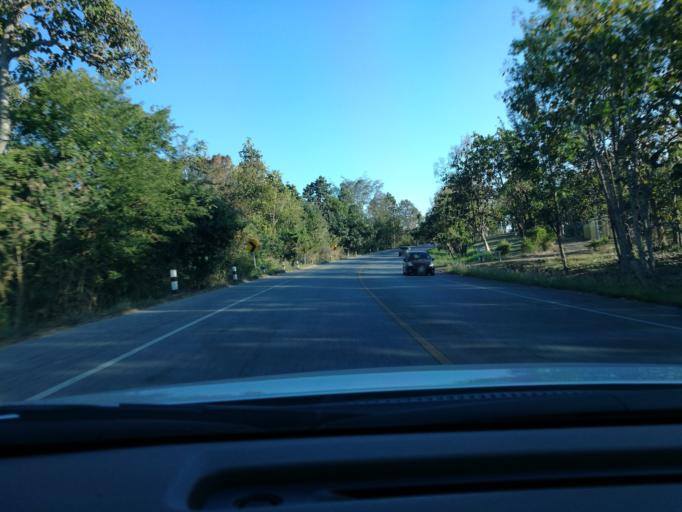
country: TH
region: Phitsanulok
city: Nakhon Thai
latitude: 17.0350
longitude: 100.8184
